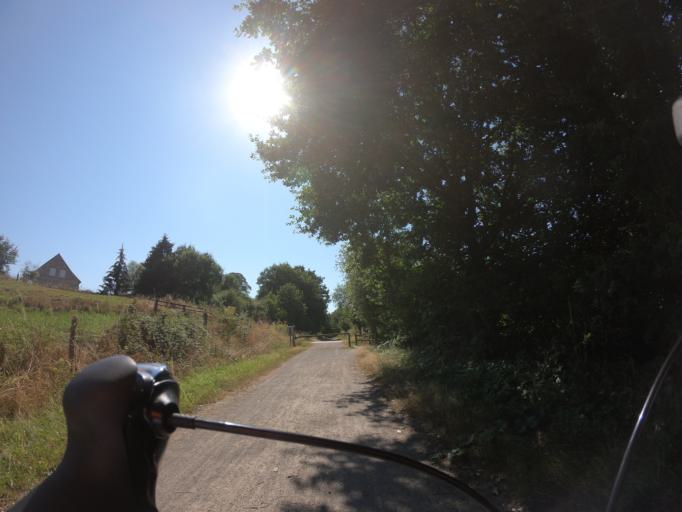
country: FR
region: Lower Normandy
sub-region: Departement de la Manche
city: Barenton
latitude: 48.5897
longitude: -0.8531
